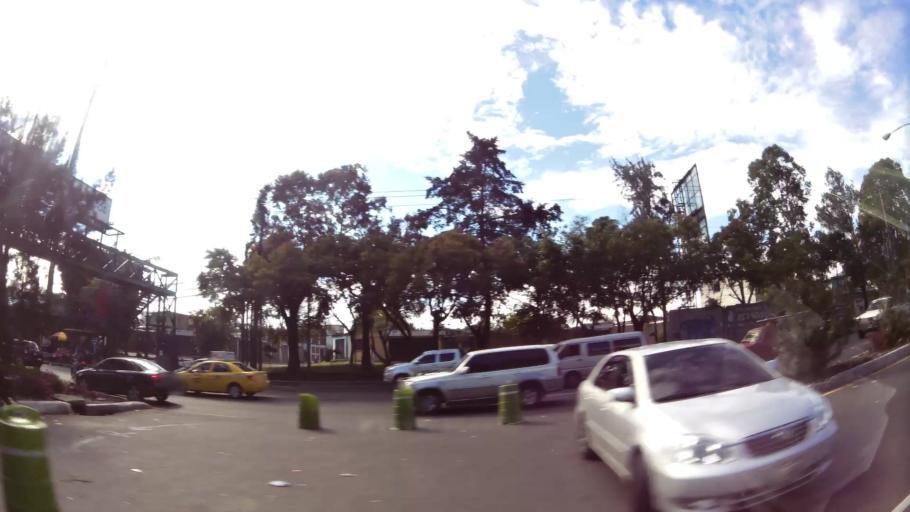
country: GT
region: Guatemala
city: Mixco
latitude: 14.6349
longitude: -90.5938
